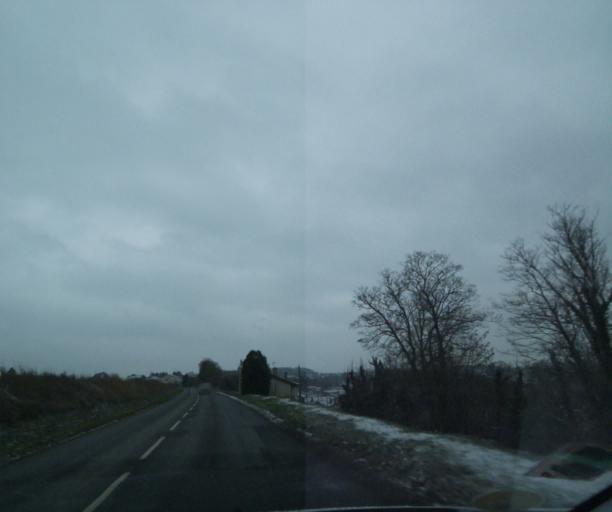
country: FR
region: Champagne-Ardenne
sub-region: Departement de la Haute-Marne
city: Wassy
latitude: 48.4320
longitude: 4.9620
